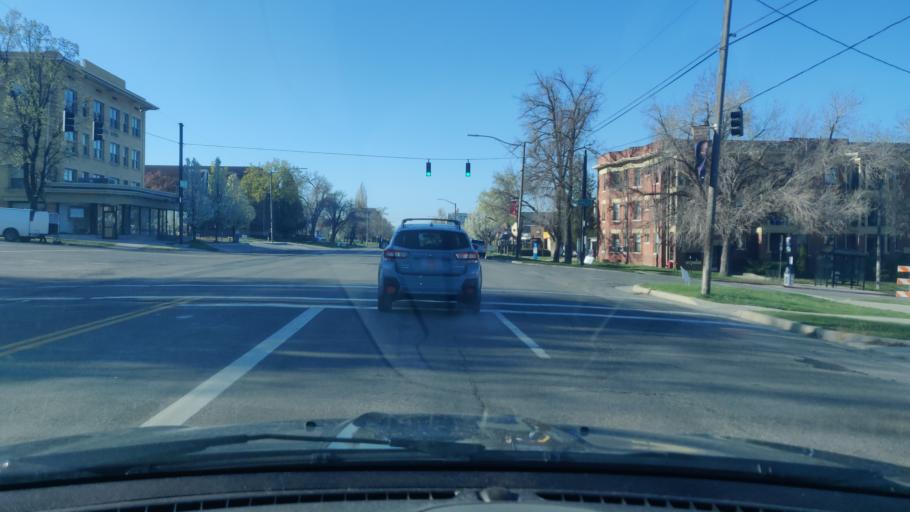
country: US
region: Utah
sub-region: Salt Lake County
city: Salt Lake City
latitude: 40.7653
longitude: -111.8540
